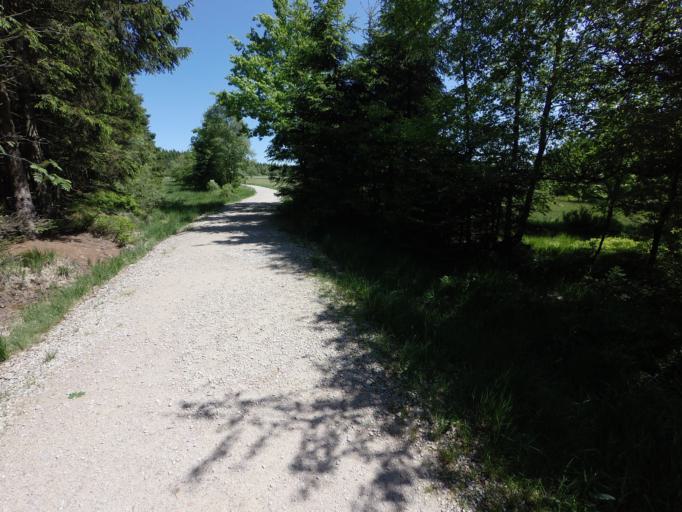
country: BE
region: Wallonia
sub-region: Province de Liege
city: Malmedy
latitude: 50.5098
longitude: 6.0655
